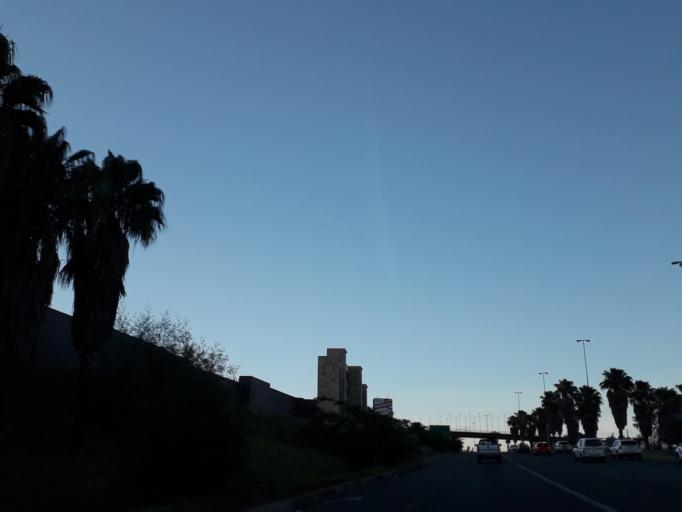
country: ZA
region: Gauteng
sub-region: City of Johannesburg Metropolitan Municipality
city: Roodepoort
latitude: -26.1484
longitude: 27.9233
